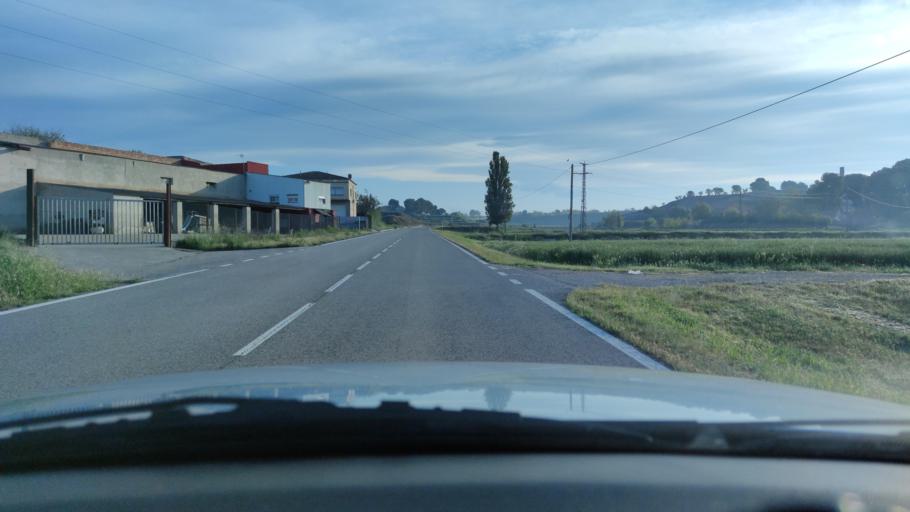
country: ES
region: Catalonia
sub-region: Provincia de Lleida
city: Castellsera
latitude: 41.7578
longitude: 0.9958
